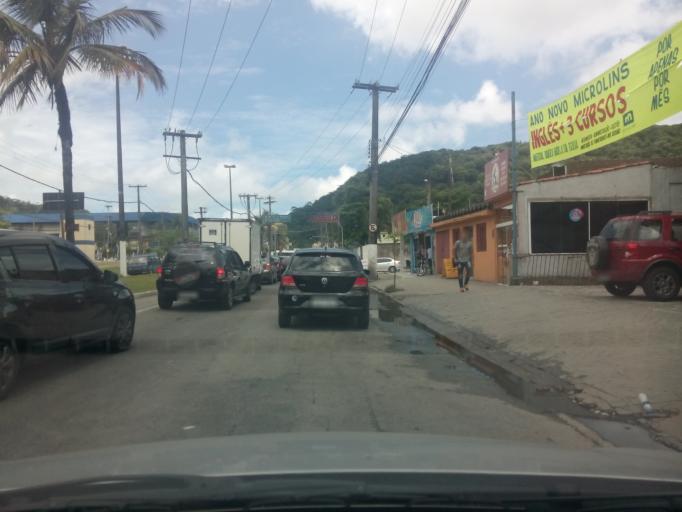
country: BR
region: Sao Paulo
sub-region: Guaruja
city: Guaruja
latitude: -23.9856
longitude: -46.2663
